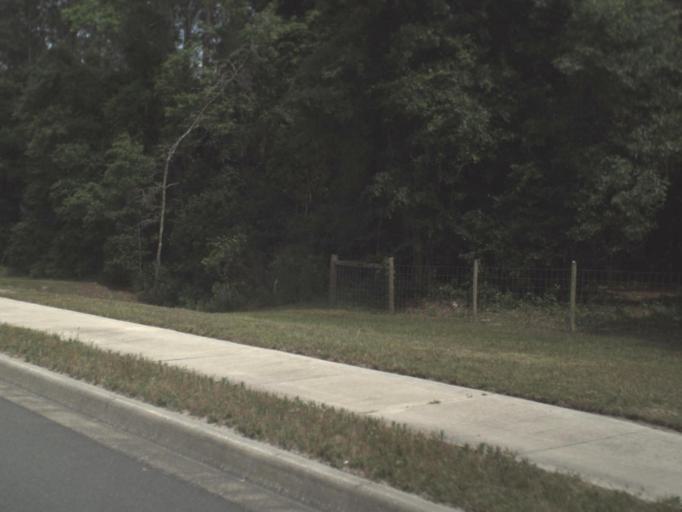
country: US
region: Florida
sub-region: Putnam County
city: Interlachen
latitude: 29.6271
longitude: -81.8531
